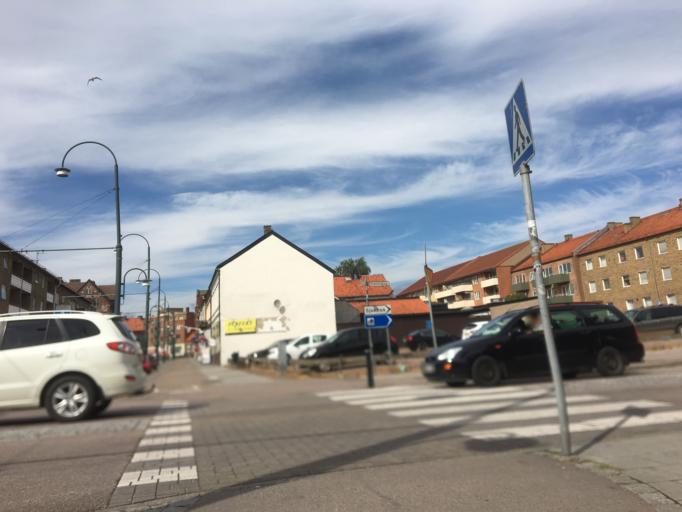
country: SE
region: Skane
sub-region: Landskrona
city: Landskrona
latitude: 55.8767
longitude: 12.8331
